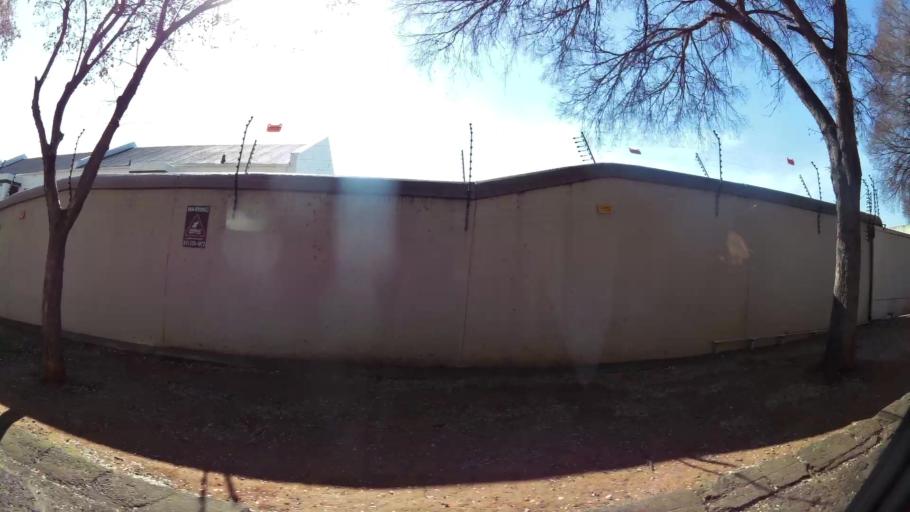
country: ZA
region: Gauteng
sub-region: City of Johannesburg Metropolitan Municipality
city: Roodepoort
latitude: -26.1192
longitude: 27.9625
